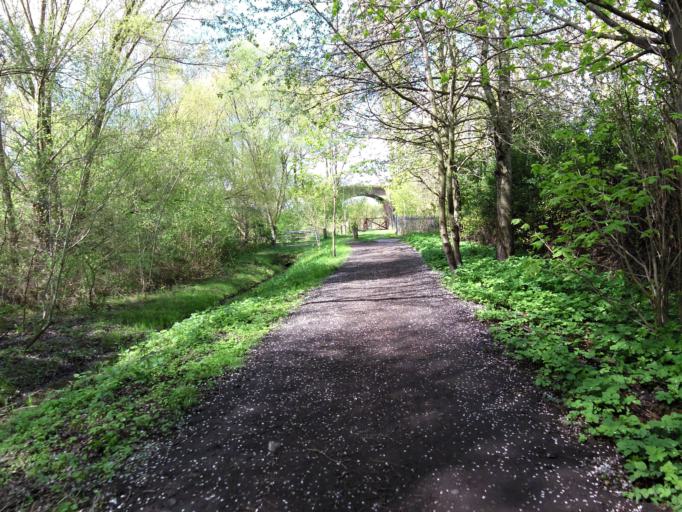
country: DE
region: Saxony
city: Leipzig
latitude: 51.3418
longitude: 12.4236
